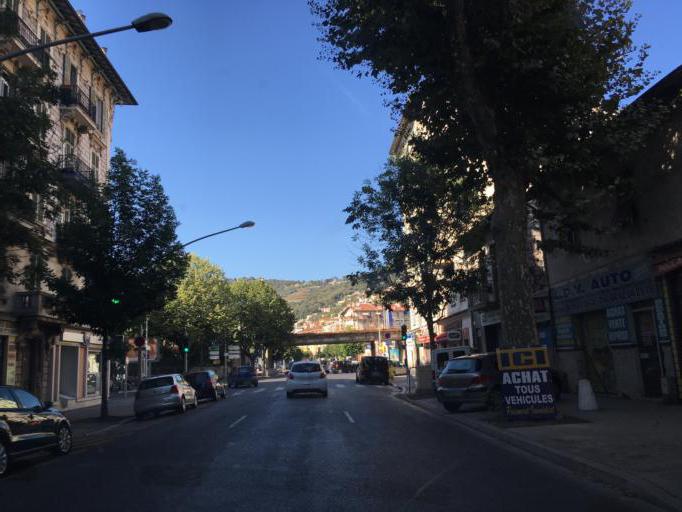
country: FR
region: Provence-Alpes-Cote d'Azur
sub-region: Departement des Alpes-Maritimes
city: Villefranche-sur-Mer
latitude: 43.7046
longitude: 7.2905
